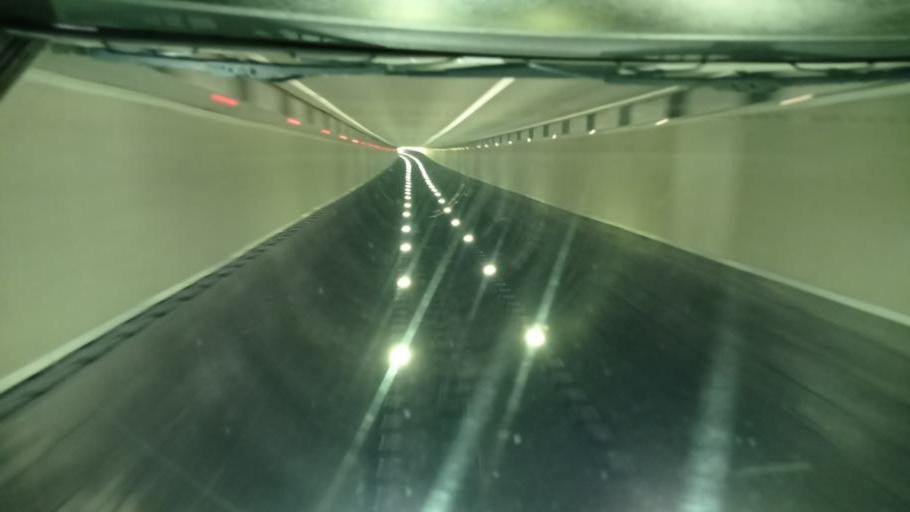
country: RU
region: Krasnodarskiy
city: Vysokoye
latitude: 43.5191
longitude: 39.9936
